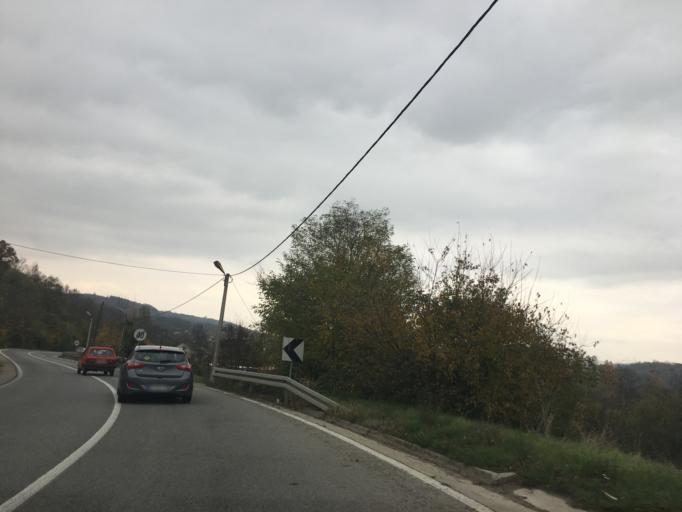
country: RS
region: Central Serbia
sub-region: Raski Okrug
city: Kraljevo
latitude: 43.7166
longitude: 20.7973
